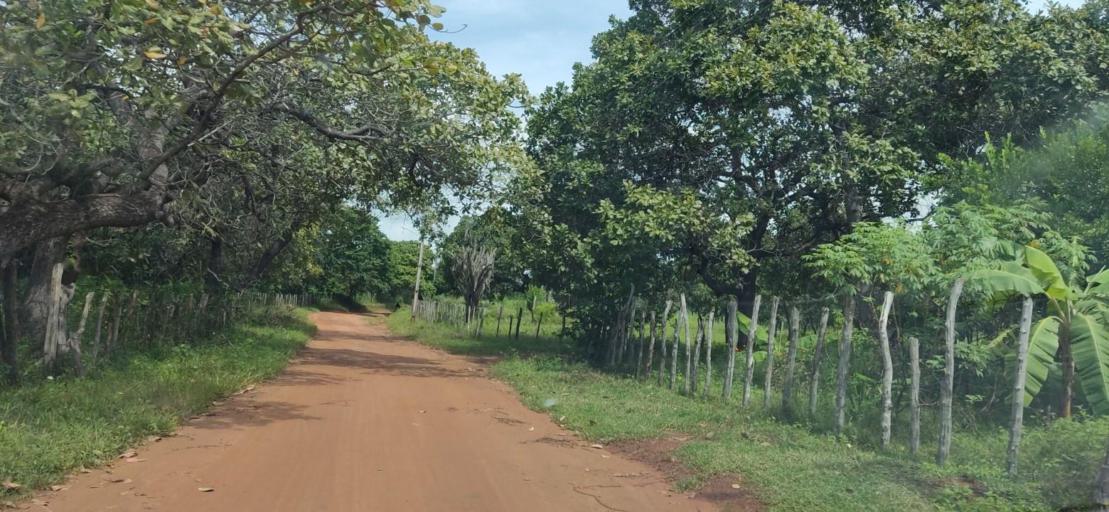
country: BR
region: Piaui
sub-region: Valenca Do Piaui
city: Valenca do Piaui
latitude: -6.1096
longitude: -41.8024
